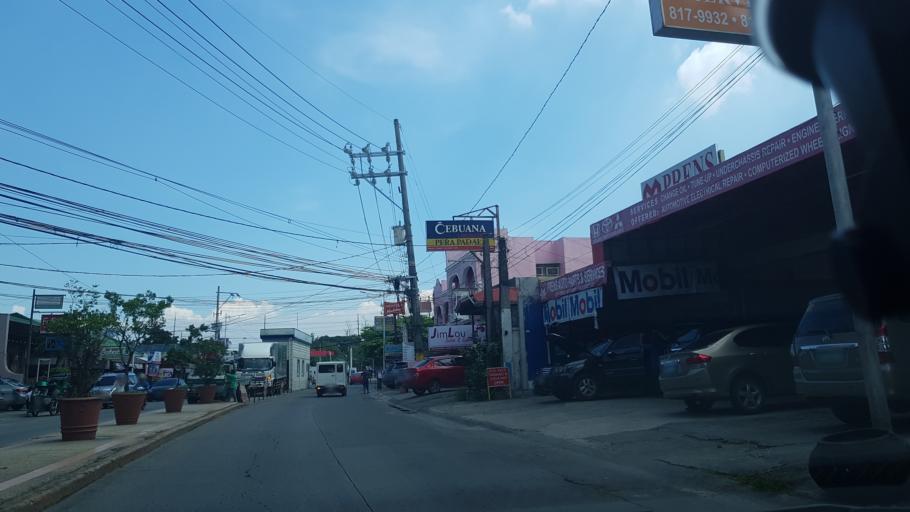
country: PH
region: Calabarzon
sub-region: Province of Rizal
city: Las Pinas
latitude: 14.4427
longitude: 120.9920
